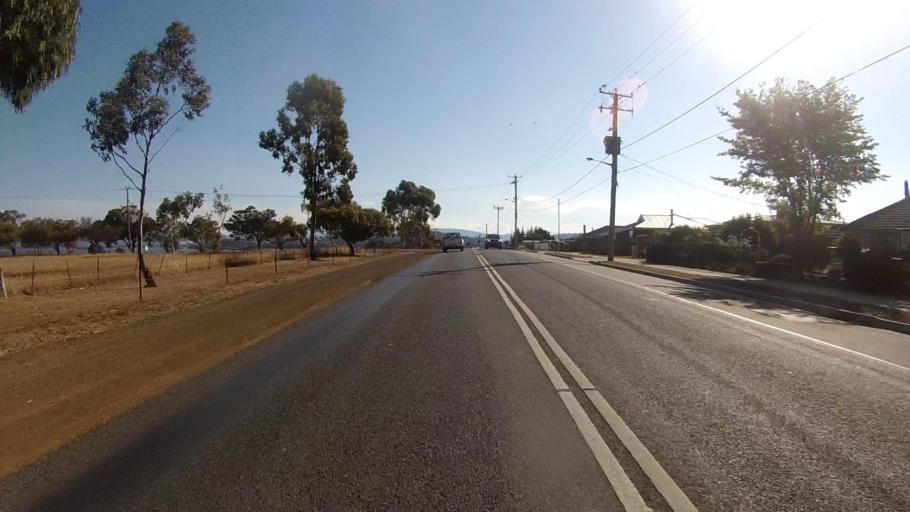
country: AU
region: Tasmania
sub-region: Sorell
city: Sorell
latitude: -42.7915
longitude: 147.5595
